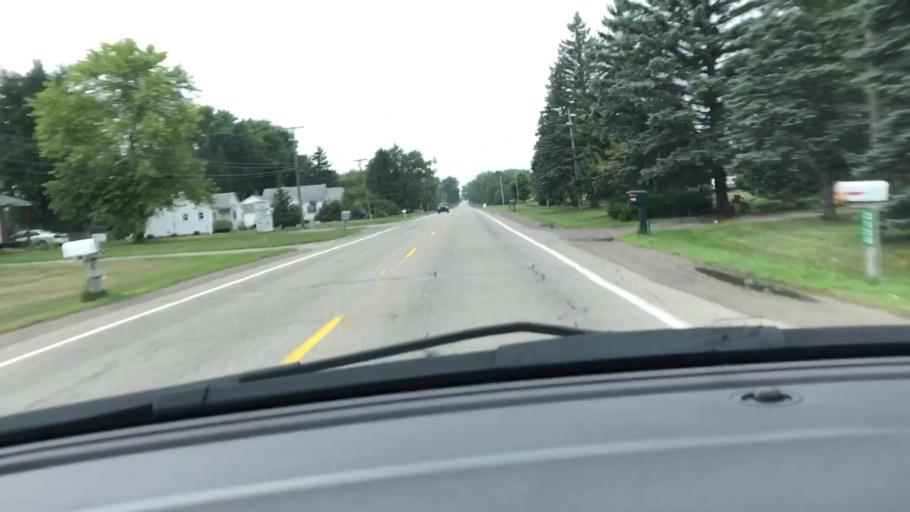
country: US
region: Michigan
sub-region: Bay County
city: Auburn
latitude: 43.6044
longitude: -84.1339
